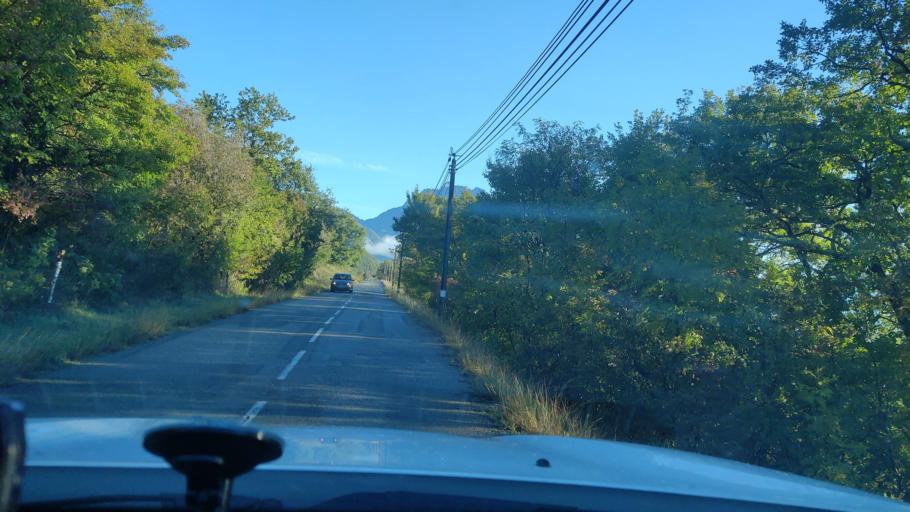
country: FR
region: Rhone-Alpes
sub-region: Departement de la Savoie
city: Cruet
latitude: 45.5325
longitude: 6.1018
